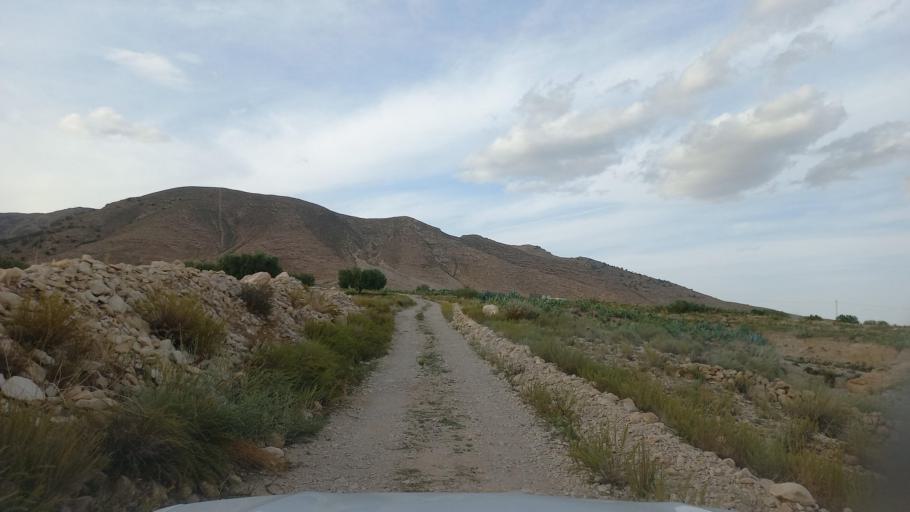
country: TN
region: Al Qasrayn
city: Sbiba
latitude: 35.4484
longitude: 9.0665
